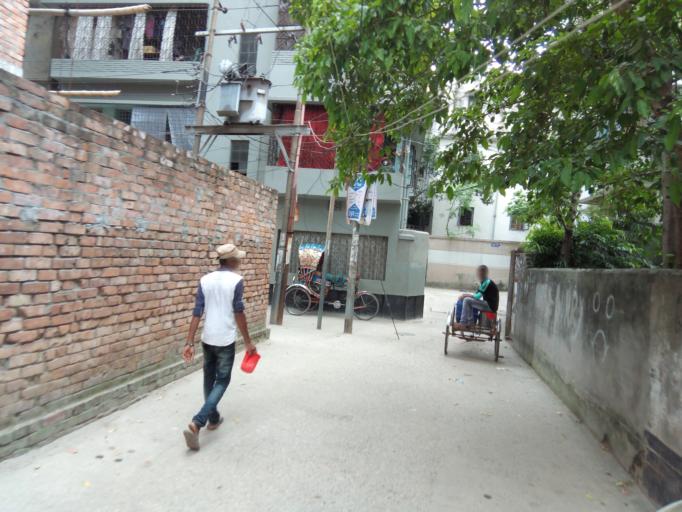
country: BD
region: Dhaka
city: Paltan
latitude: 23.7309
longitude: 90.4236
